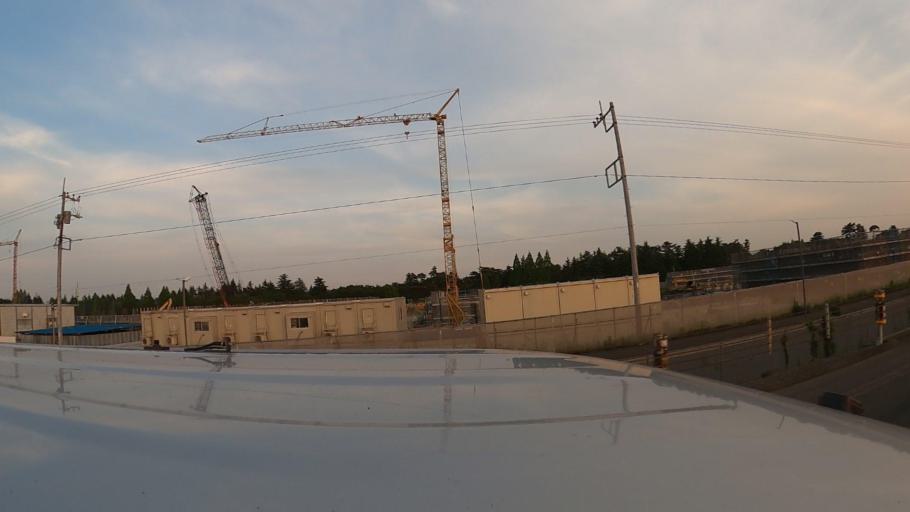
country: JP
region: Ibaraki
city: Mitsukaido
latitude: 36.0120
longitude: 140.0508
